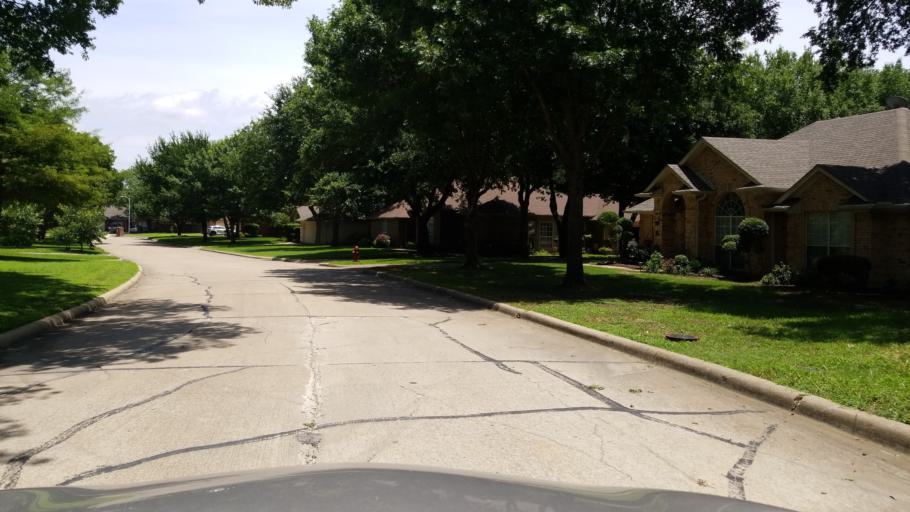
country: US
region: Texas
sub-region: Dallas County
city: Grand Prairie
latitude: 32.6831
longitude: -96.9873
